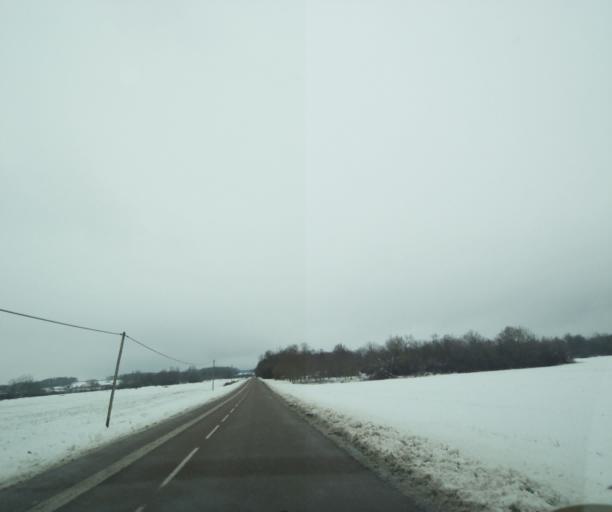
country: FR
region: Champagne-Ardenne
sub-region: Departement de la Haute-Marne
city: Montier-en-Der
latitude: 48.4497
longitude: 4.7810
